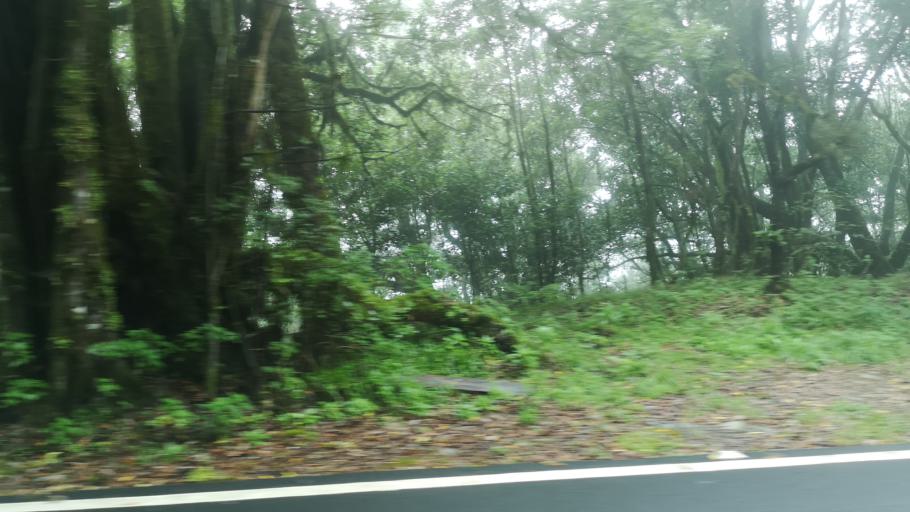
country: ES
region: Canary Islands
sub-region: Provincia de Santa Cruz de Tenerife
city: Alajero
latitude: 28.1095
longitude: -17.2201
